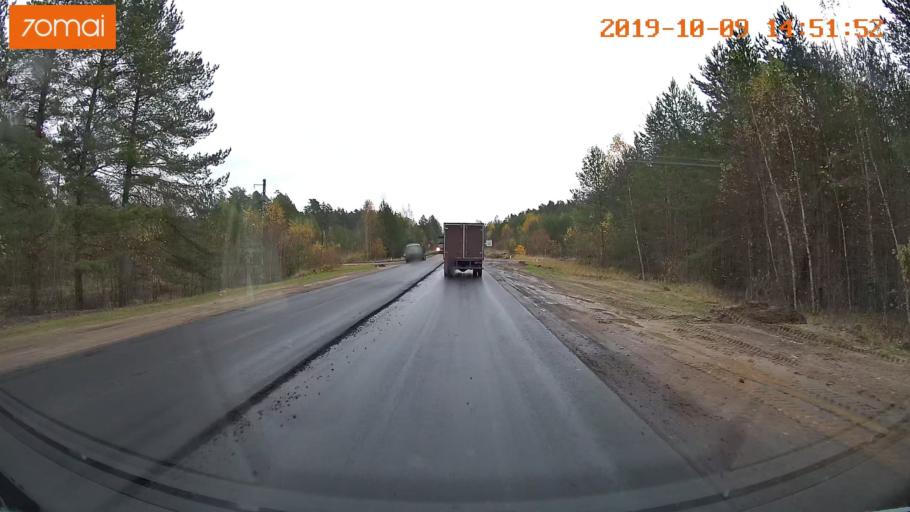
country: RU
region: Kostroma
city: Chistyye Bory
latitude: 58.3773
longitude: 41.6190
